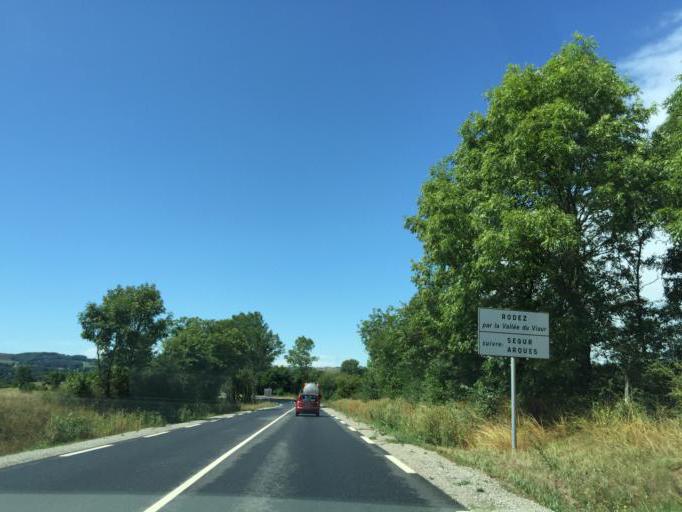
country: FR
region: Midi-Pyrenees
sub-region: Departement de l'Aveyron
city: Severac-le-Chateau
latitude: 44.2410
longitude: 2.9517
